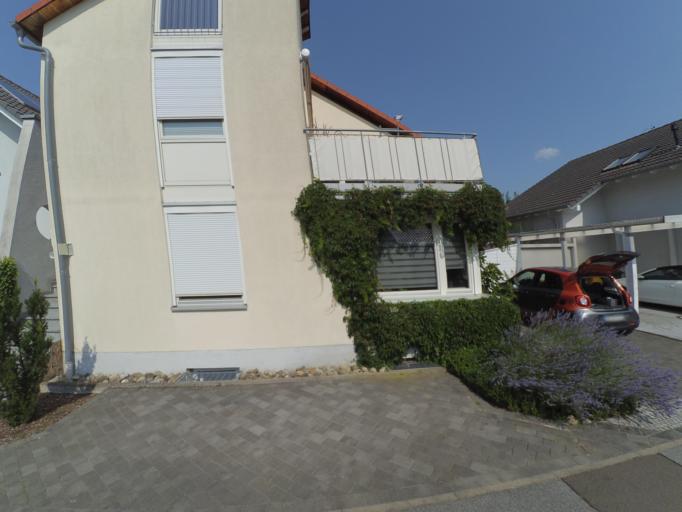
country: DE
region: Hesse
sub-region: Regierungsbezirk Darmstadt
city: Burstadt
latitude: 49.6394
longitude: 8.4702
